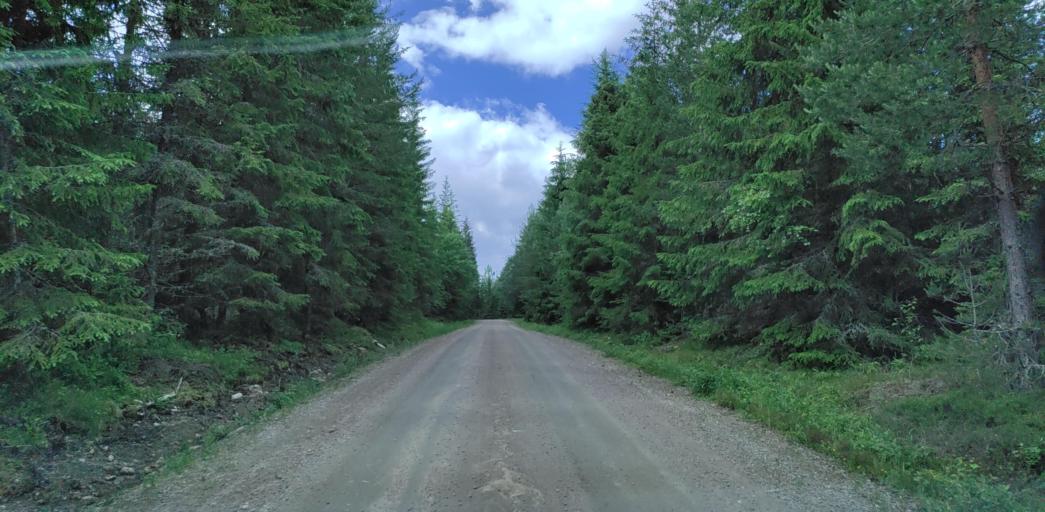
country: SE
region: Vaermland
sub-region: Hagfors Kommun
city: Ekshaerad
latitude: 60.1017
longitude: 13.3847
